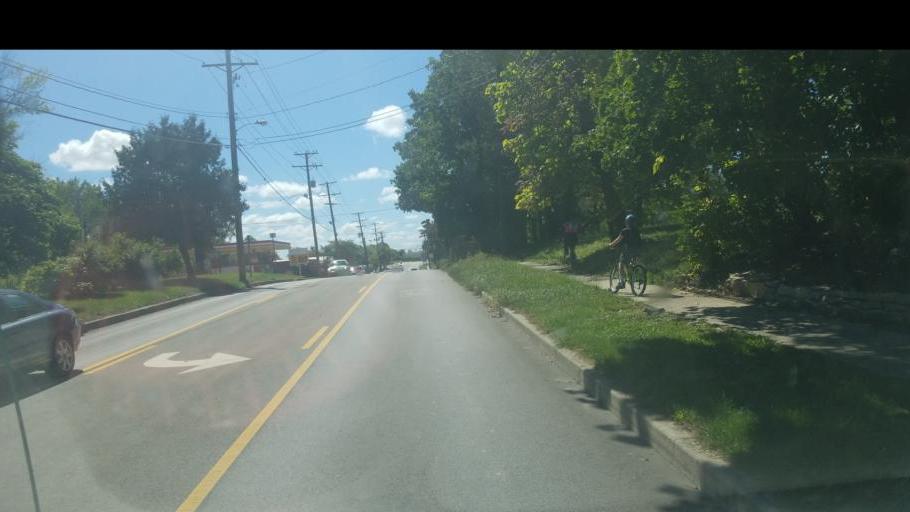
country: US
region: Ohio
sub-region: Delaware County
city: Delaware
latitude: 40.2842
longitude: -83.0690
